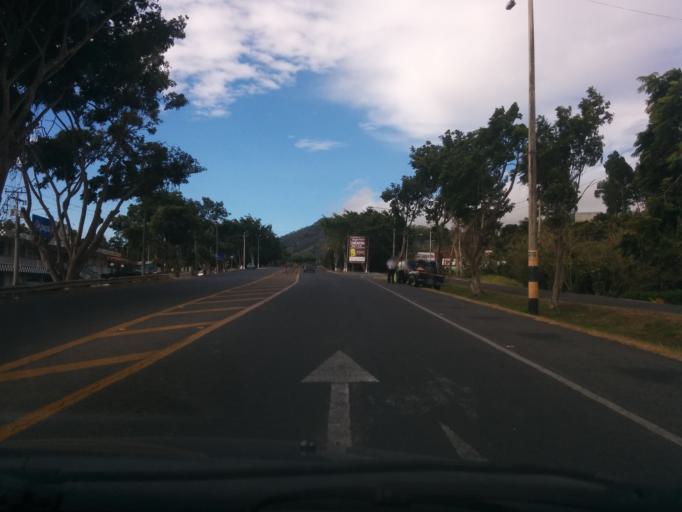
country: CR
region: Alajuela
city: Esquipulas
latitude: 10.0642
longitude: -84.4421
